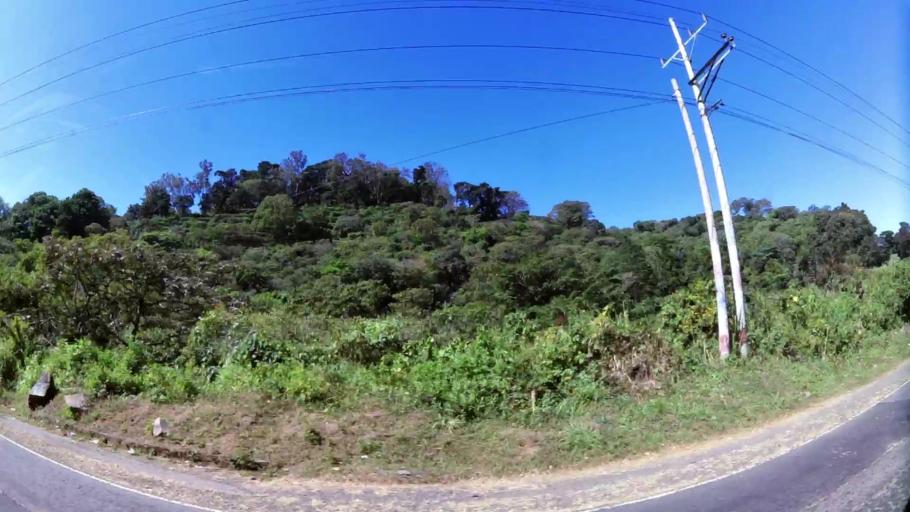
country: SV
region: Ahuachapan
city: Concepcion de Ataco
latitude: 13.8609
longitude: -89.8426
